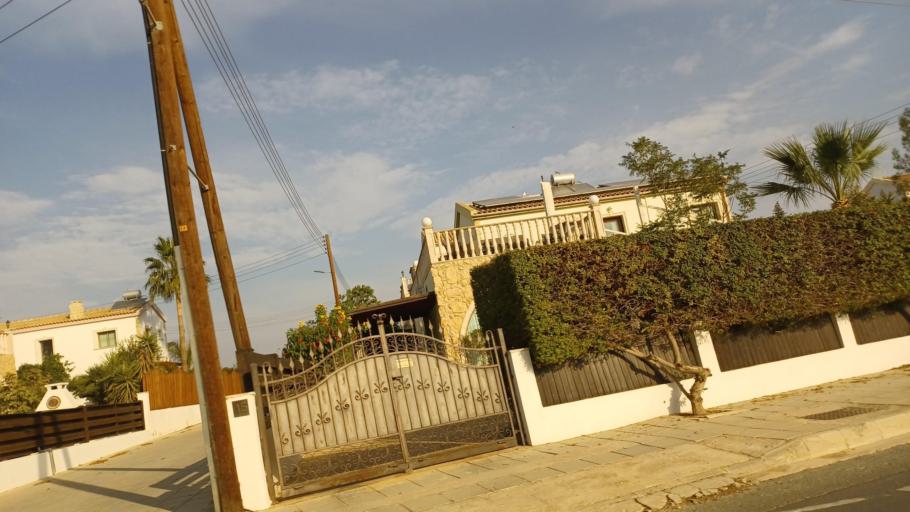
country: CY
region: Ammochostos
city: Acheritou
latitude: 35.0730
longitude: 33.8762
